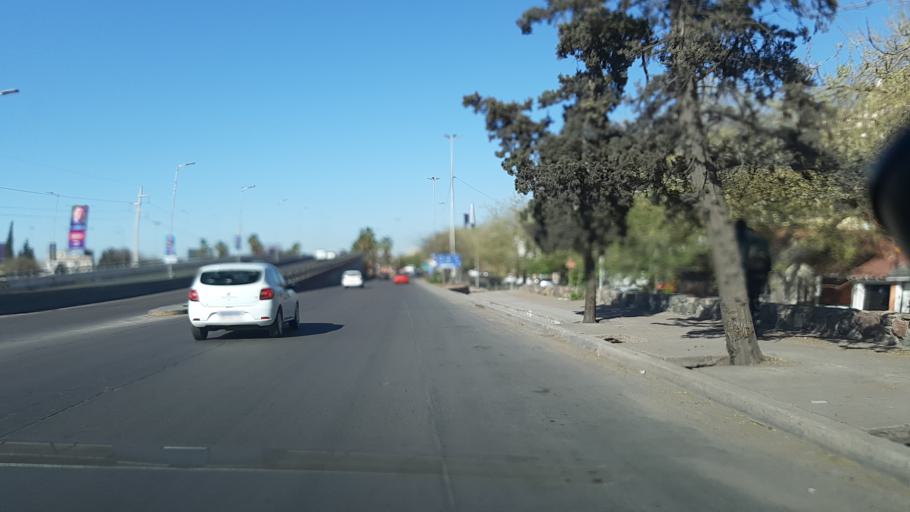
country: AR
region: Mendoza
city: Mendoza
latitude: -32.8938
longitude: -68.8318
